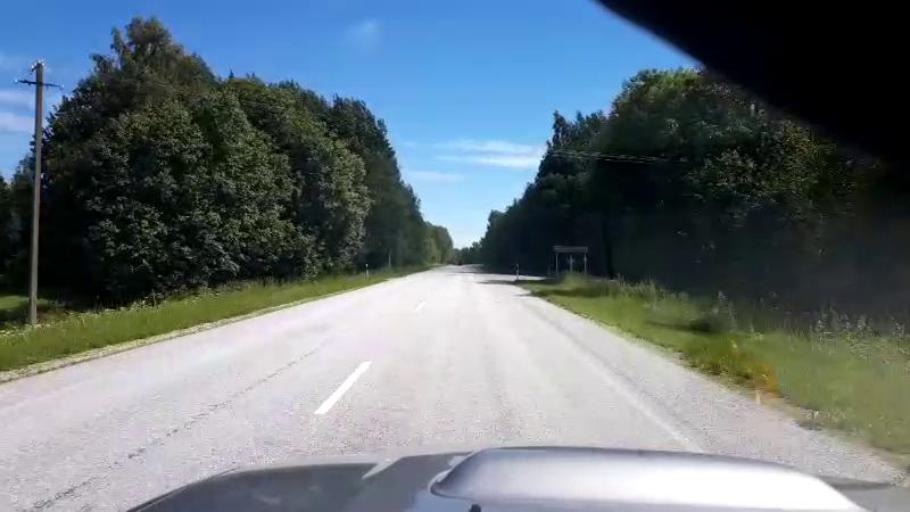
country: EE
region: Laeaene-Virumaa
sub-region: Rakke vald
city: Rakke
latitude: 58.9504
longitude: 26.1799
